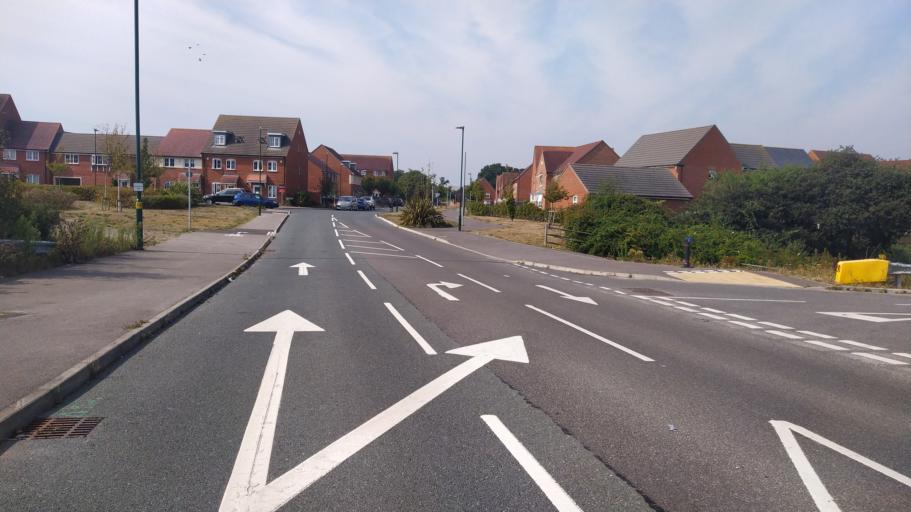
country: GB
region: England
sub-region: West Sussex
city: Barnham
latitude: 50.8026
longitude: -0.6455
